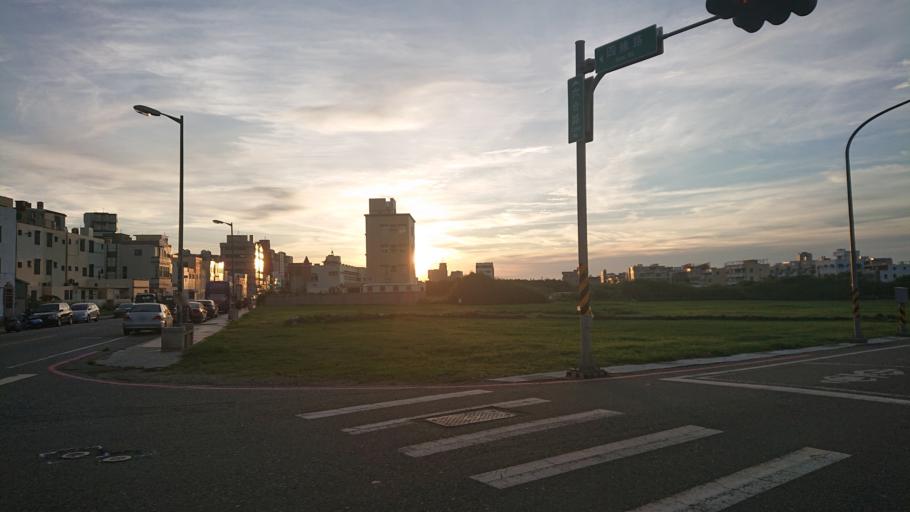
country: TW
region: Taiwan
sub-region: Penghu
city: Ma-kung
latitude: 23.5757
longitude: 119.5807
